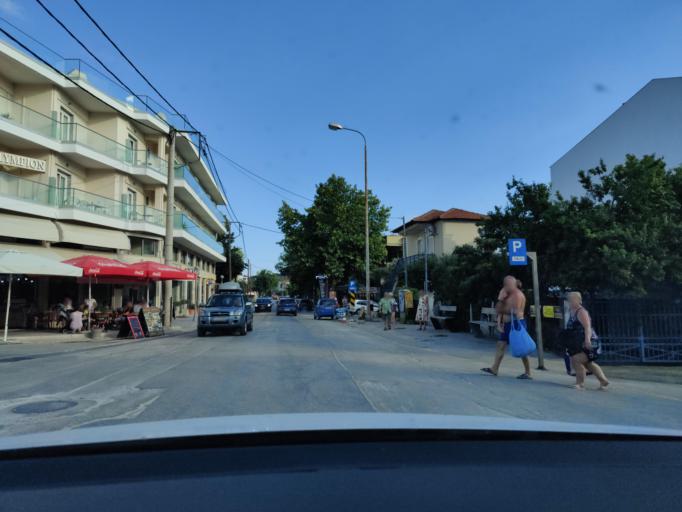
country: GR
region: East Macedonia and Thrace
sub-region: Nomos Kavalas
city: Limenaria
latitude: 40.6105
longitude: 24.6074
